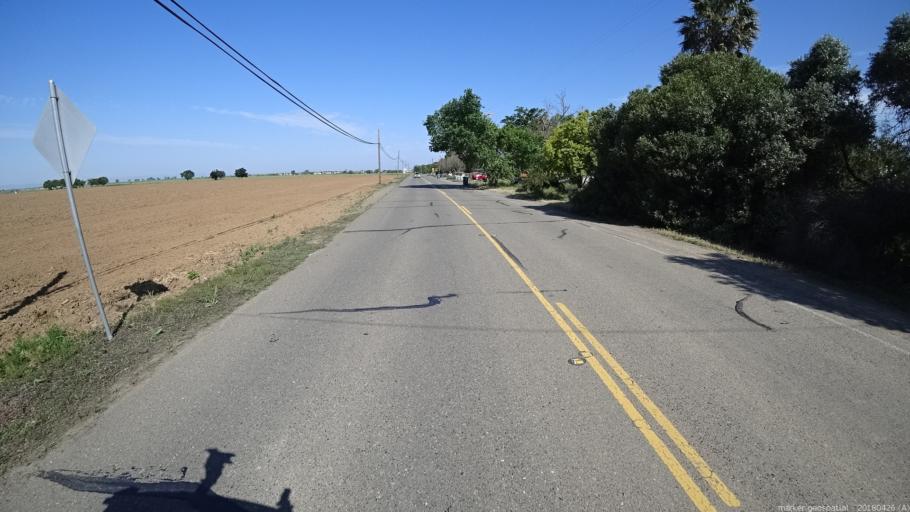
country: US
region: California
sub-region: Yolo County
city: West Sacramento
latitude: 38.5171
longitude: -121.5536
